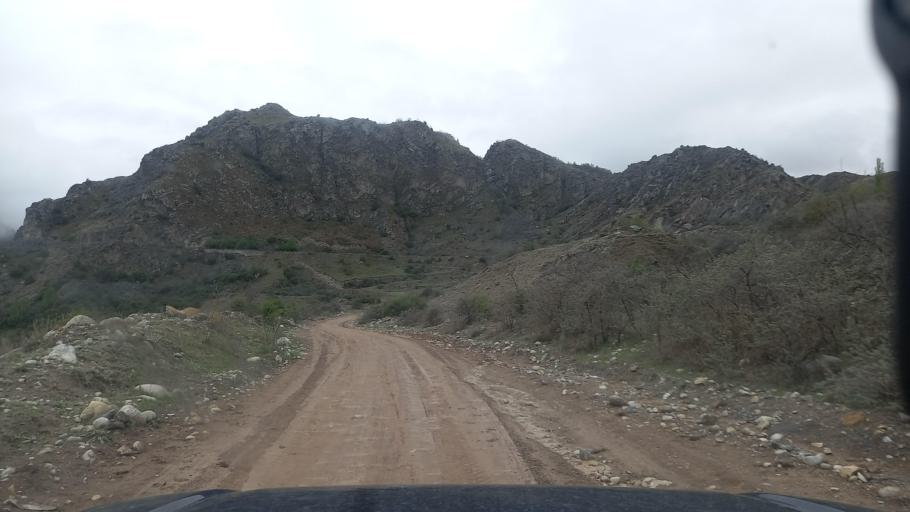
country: RU
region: Kabardino-Balkariya
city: Bylym
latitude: 43.4578
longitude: 43.0100
